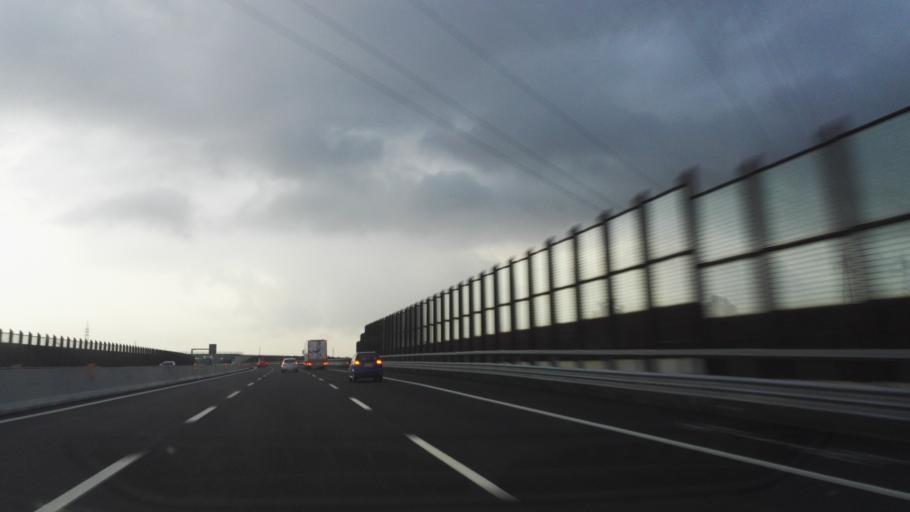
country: IT
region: Lombardy
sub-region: Citta metropolitana di Milano
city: Bellinzago Lombardo
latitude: 45.5283
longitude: 9.4399
